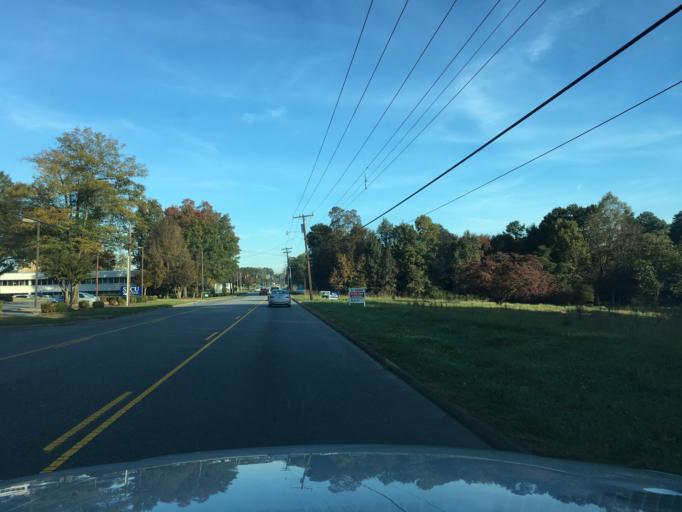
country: US
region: North Carolina
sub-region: Catawba County
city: Conover
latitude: 35.7108
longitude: -81.2646
